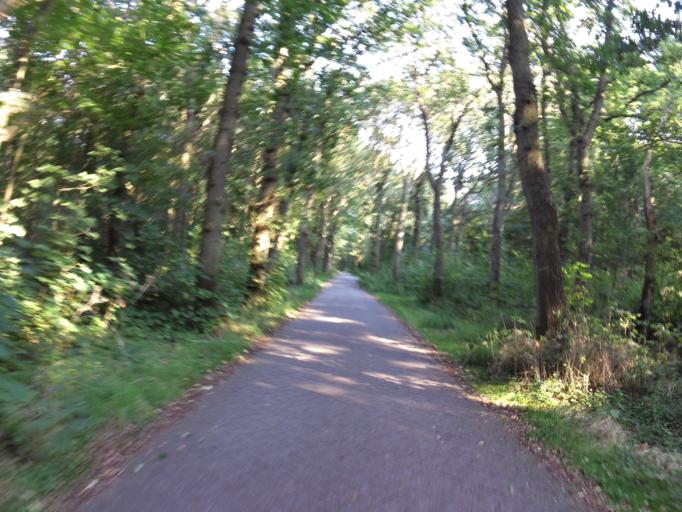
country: NL
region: North Holland
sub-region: Gemeente Castricum
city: Castricum
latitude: 52.5529
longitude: 4.6409
